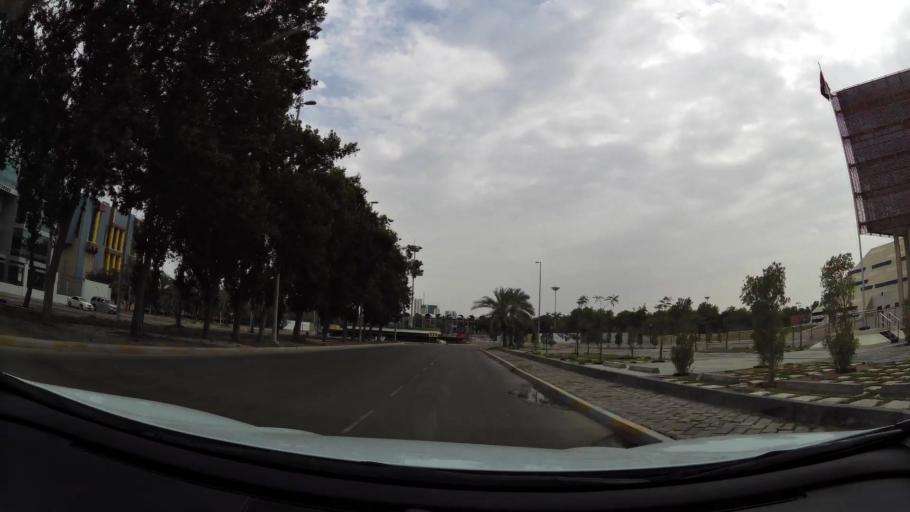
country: AE
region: Abu Dhabi
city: Abu Dhabi
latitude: 24.4179
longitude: 54.4477
